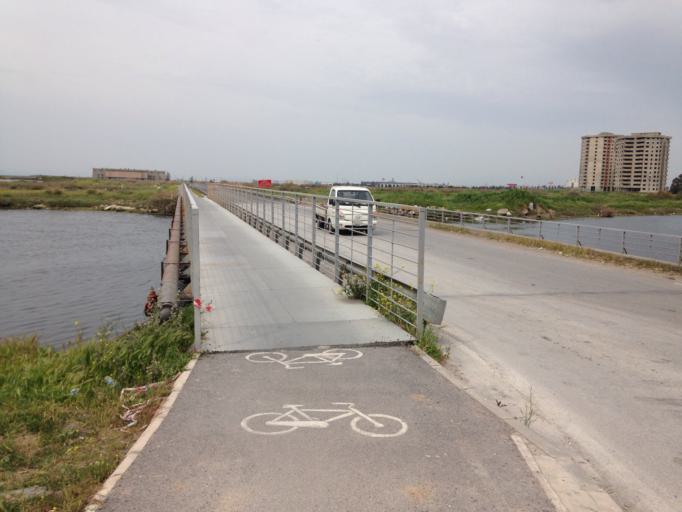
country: TR
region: Izmir
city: Karsiyaka
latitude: 38.4770
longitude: 27.0662
